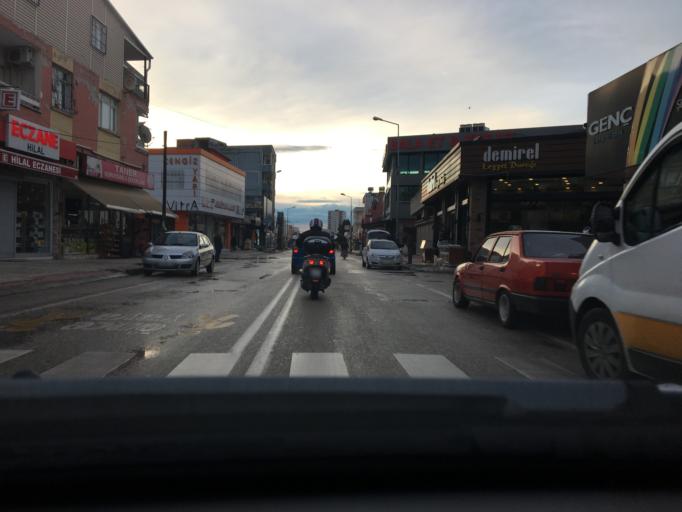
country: TR
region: Adana
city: Seyhan
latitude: 37.0170
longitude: 35.2996
